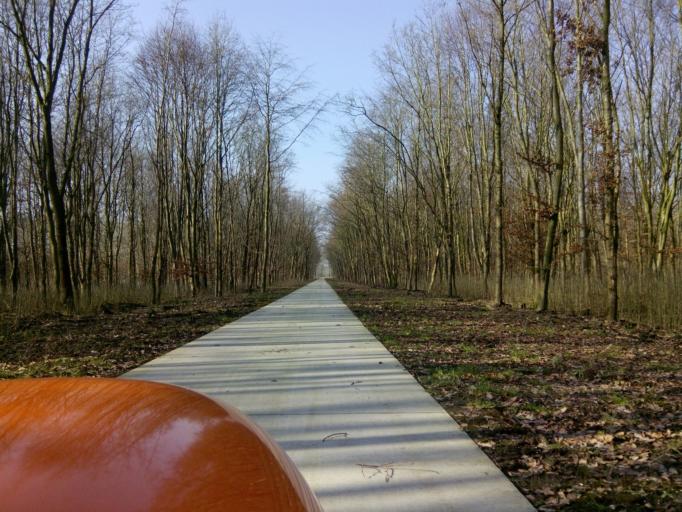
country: NL
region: Flevoland
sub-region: Gemeente Zeewolde
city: Zeewolde
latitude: 52.3207
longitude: 5.4557
